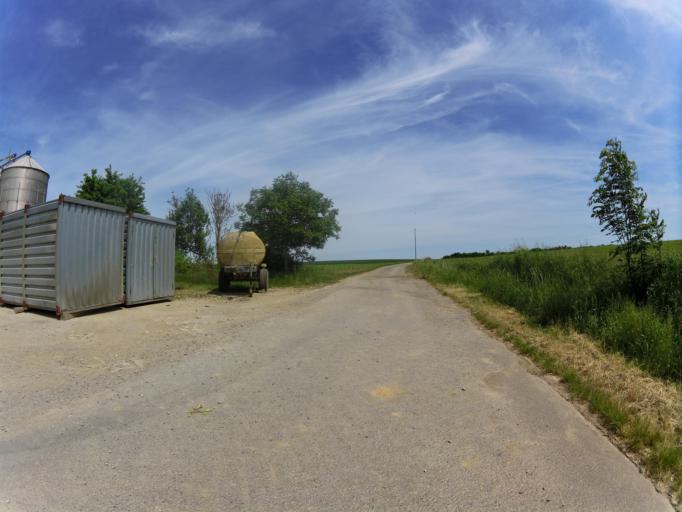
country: DE
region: Bavaria
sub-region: Regierungsbezirk Unterfranken
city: Sommerhausen
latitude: 49.6682
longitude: 10.0216
